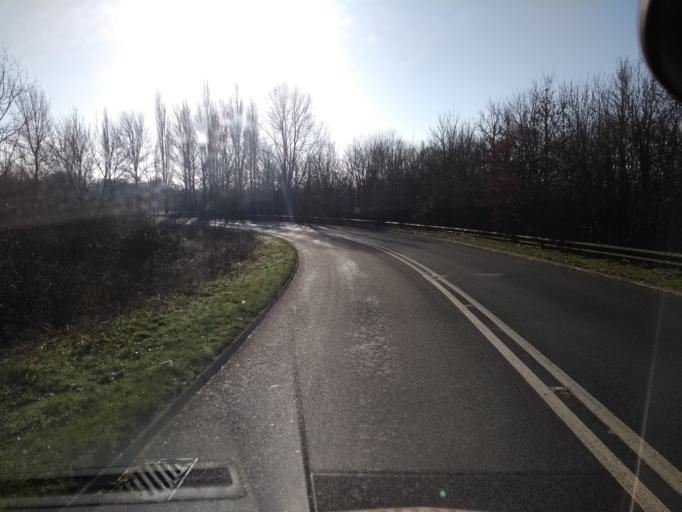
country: GB
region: England
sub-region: Somerset
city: Wincanton
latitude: 51.0475
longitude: -2.4179
